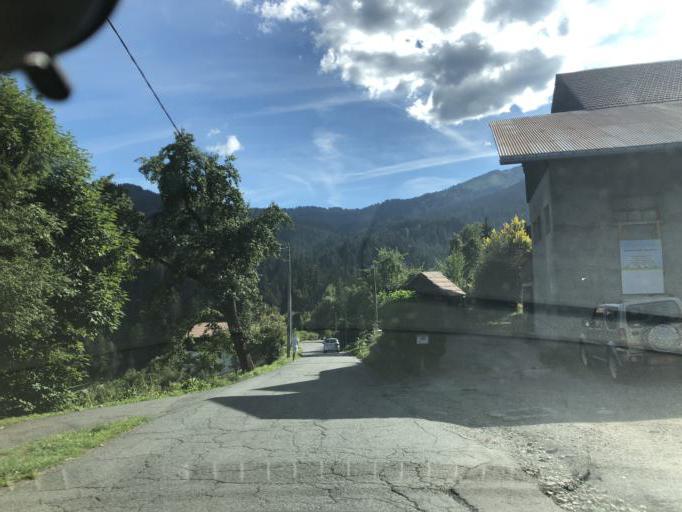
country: FR
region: Rhone-Alpes
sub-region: Departement de la Haute-Savoie
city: Cordon
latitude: 45.9106
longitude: 6.5963
